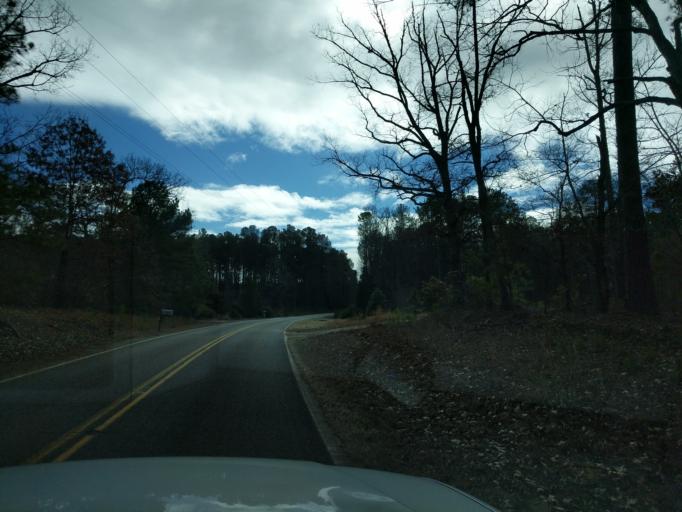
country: US
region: South Carolina
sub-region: Edgefield County
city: Edgefield
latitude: 33.8815
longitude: -81.9990
